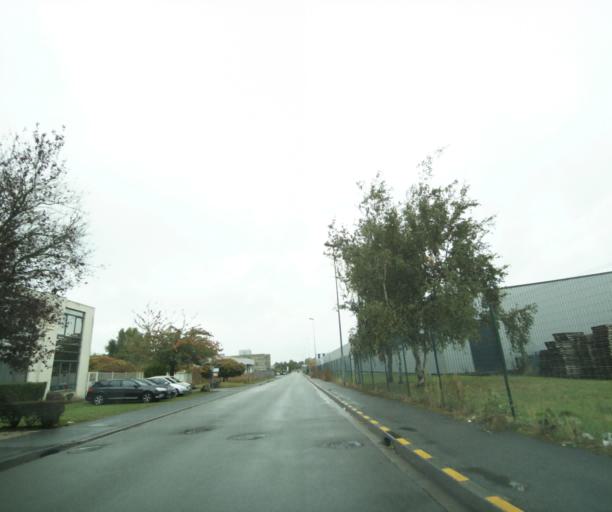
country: FR
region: Nord-Pas-de-Calais
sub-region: Departement du Nord
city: Roncq
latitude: 50.7499
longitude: 3.1377
